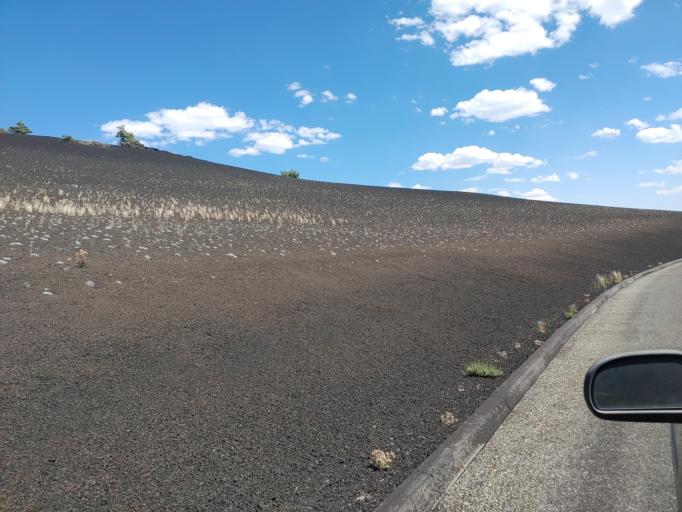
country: US
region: Idaho
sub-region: Butte County
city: Arco
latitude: 43.4415
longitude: -113.5536
